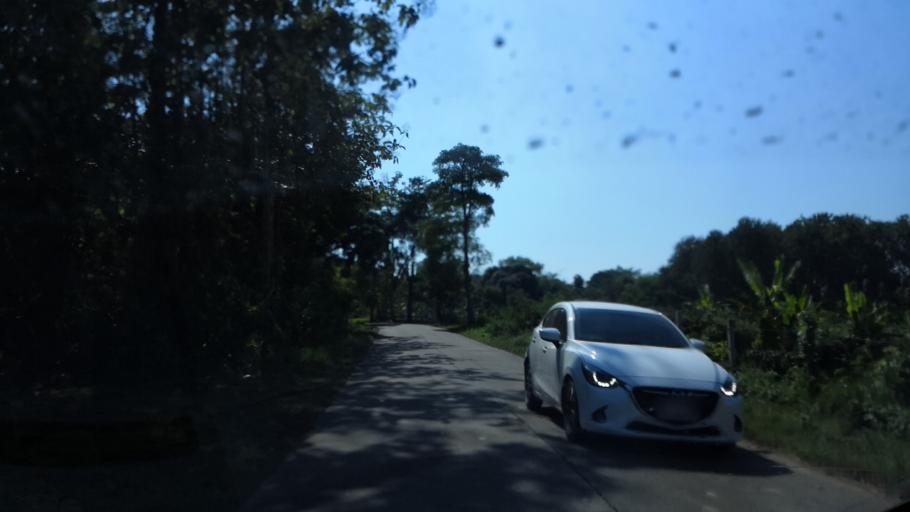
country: TH
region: Chiang Rai
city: Wiang Chai
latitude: 19.8825
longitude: 99.9421
